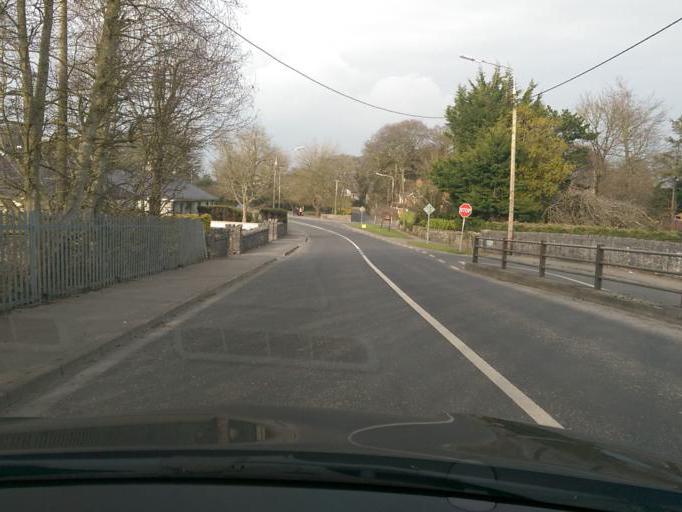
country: IE
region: Connaught
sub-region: Roscommon
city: Roscommon
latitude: 53.6228
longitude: -8.1951
